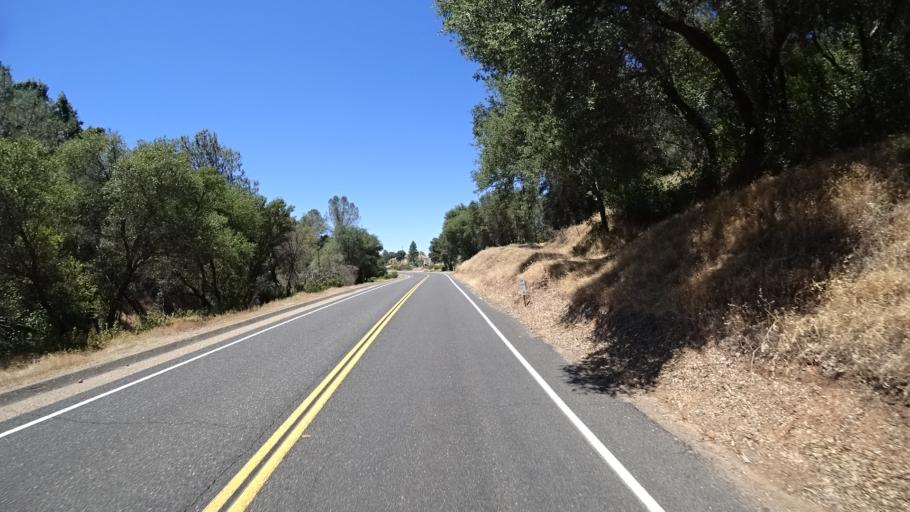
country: US
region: California
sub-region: Calaveras County
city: San Andreas
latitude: 38.1696
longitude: -120.6725
